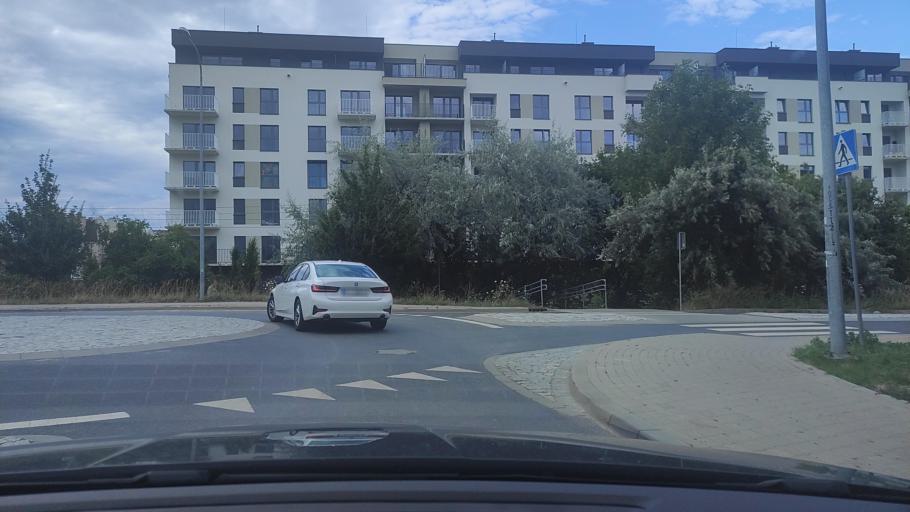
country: PL
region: Greater Poland Voivodeship
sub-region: Poznan
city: Poznan
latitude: 52.3978
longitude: 16.9577
